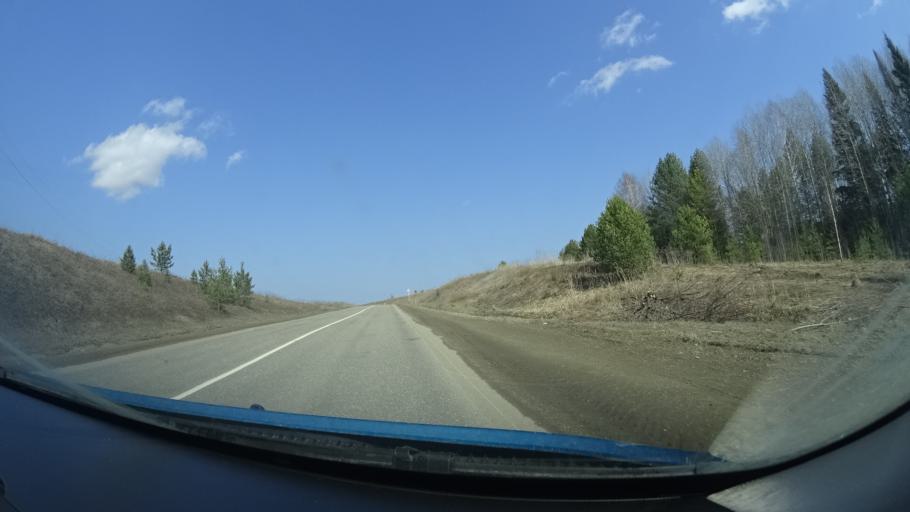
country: RU
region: Perm
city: Osa
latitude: 57.2368
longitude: 55.5953
